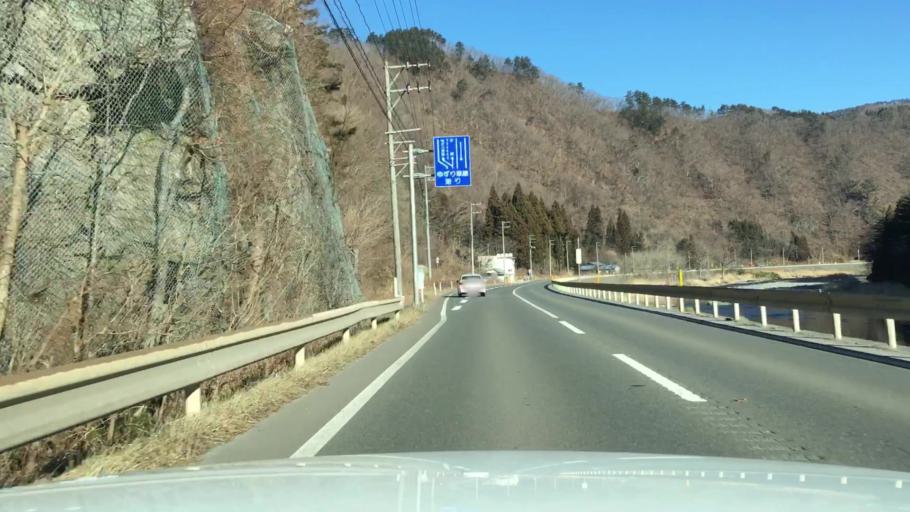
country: JP
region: Iwate
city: Miyako
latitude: 39.6128
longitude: 141.7882
